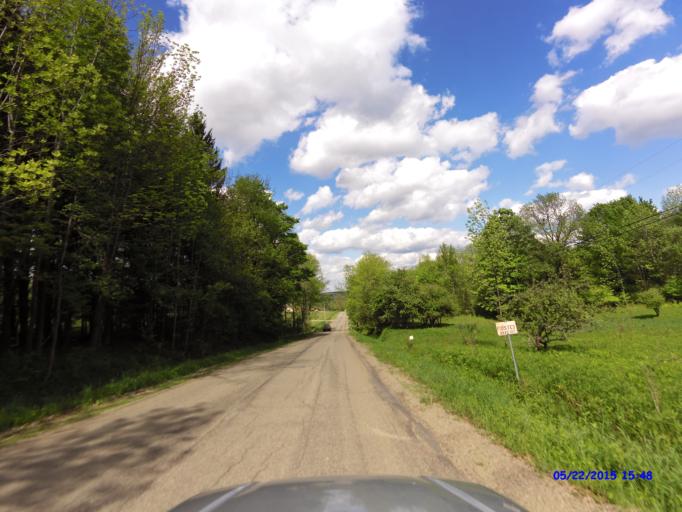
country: US
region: New York
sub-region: Cattaraugus County
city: Franklinville
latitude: 42.3323
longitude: -78.5004
